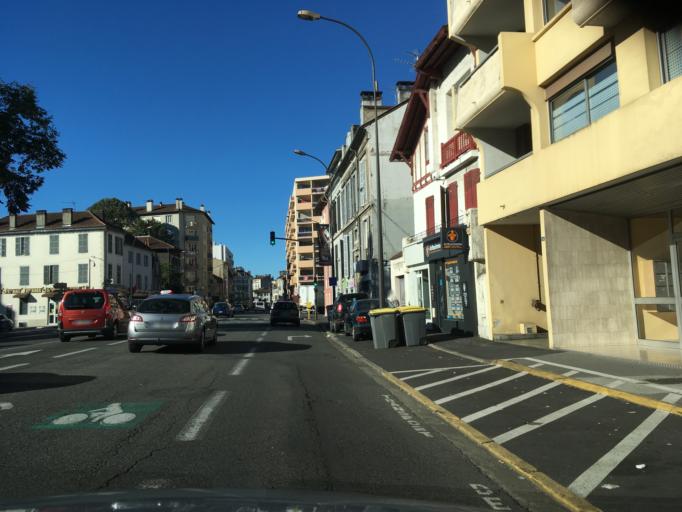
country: FR
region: Aquitaine
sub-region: Departement des Pyrenees-Atlantiques
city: Pau
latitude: 43.3018
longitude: -0.3567
